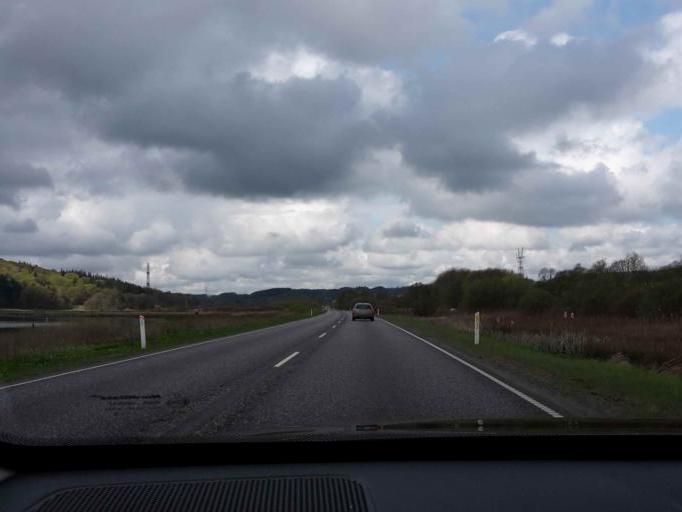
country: DK
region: South Denmark
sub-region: Vejle Kommune
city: Vejle
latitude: 55.7072
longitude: 9.4898
